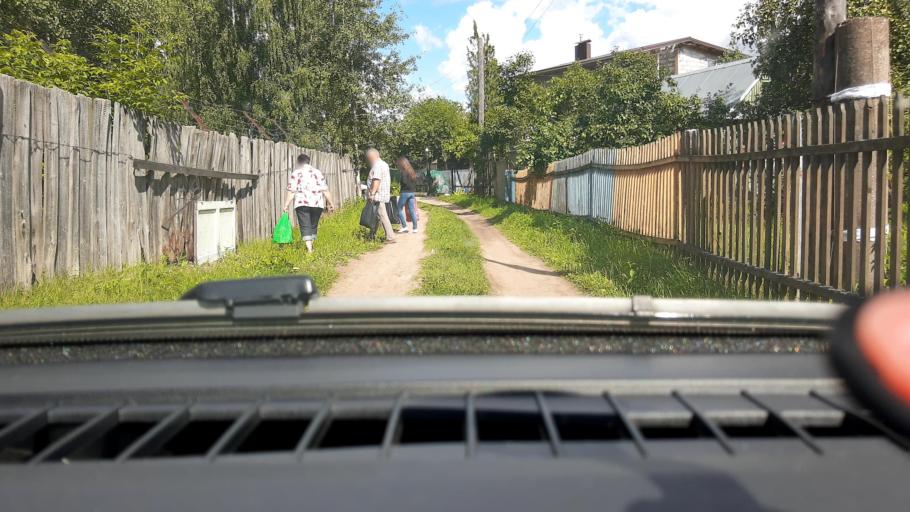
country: RU
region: Nizjnij Novgorod
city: Gorbatovka
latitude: 56.3220
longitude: 43.8274
